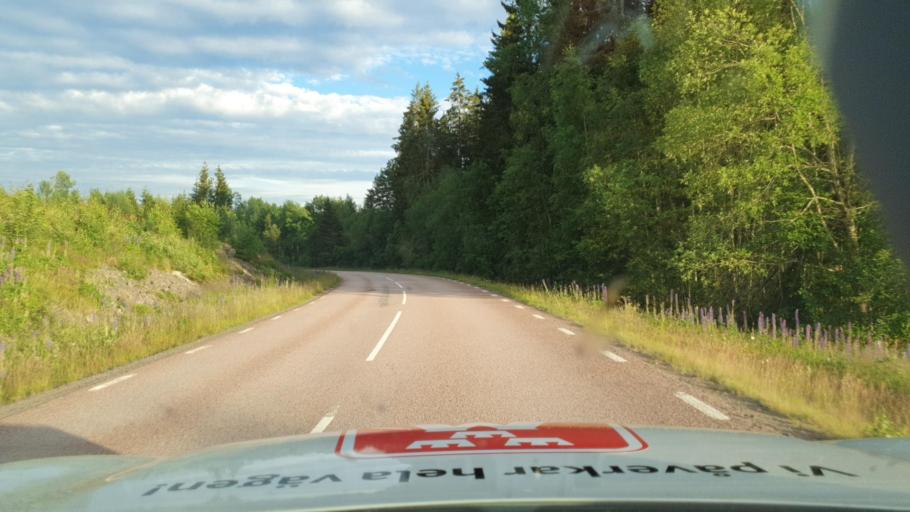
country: SE
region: Vaermland
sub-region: Karlstads Kommun
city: Molkom
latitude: 59.4879
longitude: 13.8037
